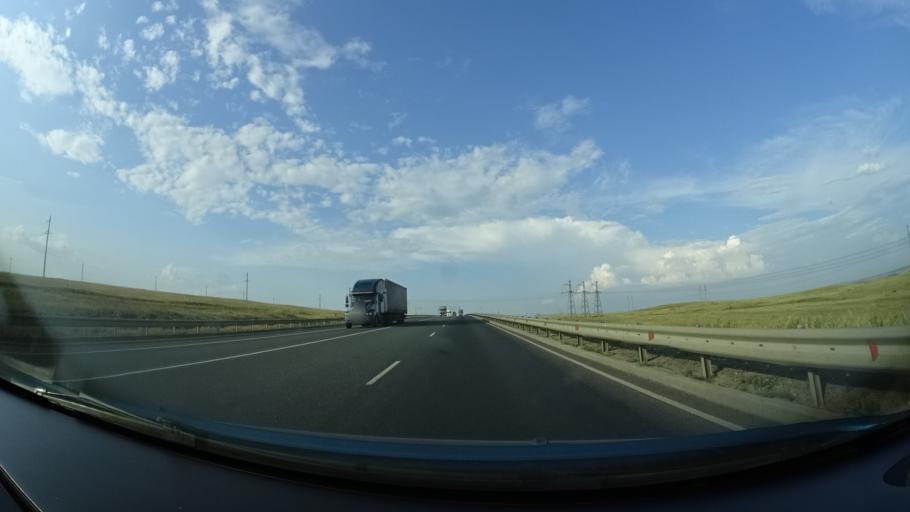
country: RU
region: Samara
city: Sukhodol
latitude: 53.6992
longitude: 50.8035
